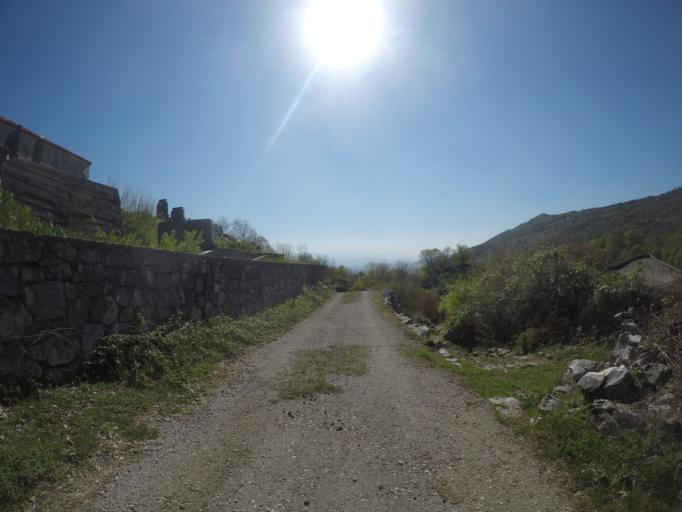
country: ME
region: Danilovgrad
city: Danilovgrad
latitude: 42.5172
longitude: 19.0558
